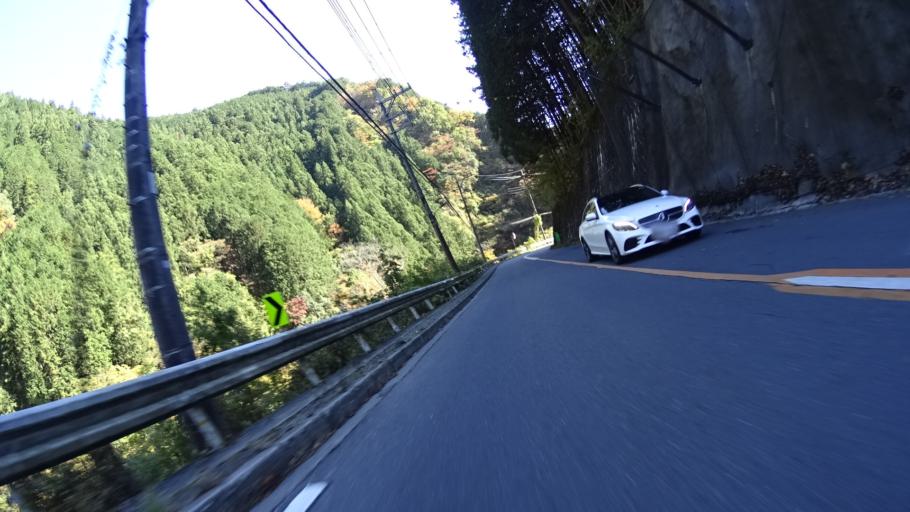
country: JP
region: Yamanashi
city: Uenohara
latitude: 35.7170
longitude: 139.0741
